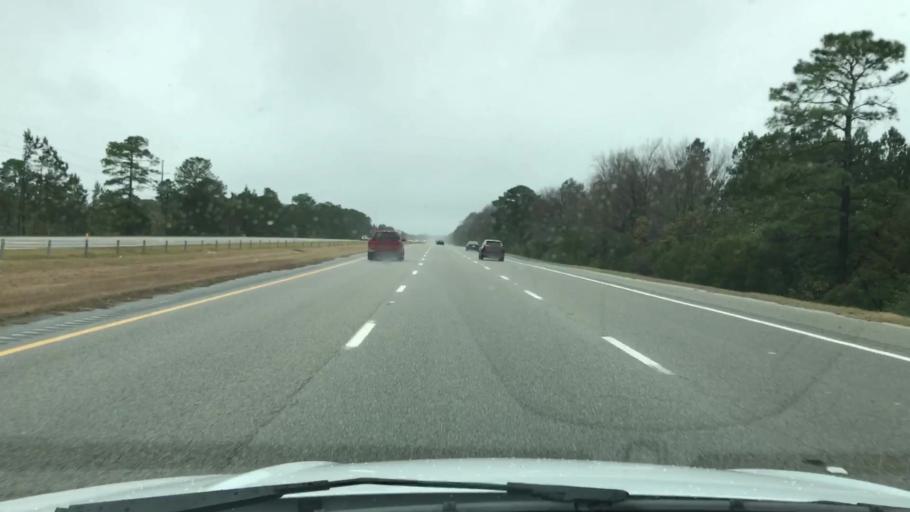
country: US
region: South Carolina
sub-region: Horry County
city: Myrtle Beach
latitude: 33.7501
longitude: -78.9003
